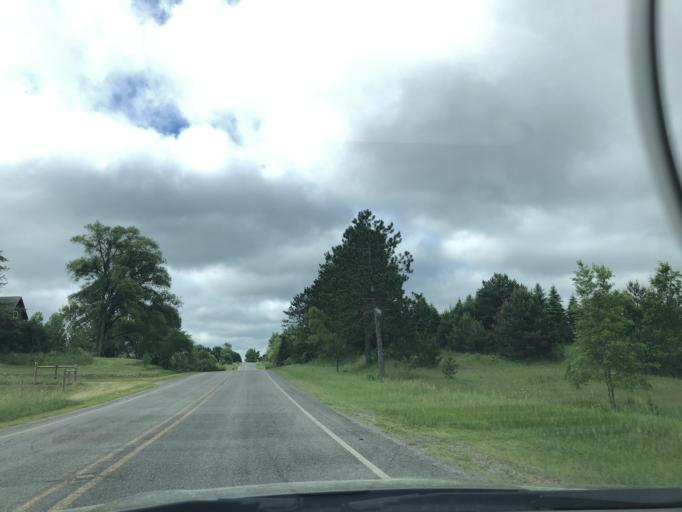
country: US
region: Michigan
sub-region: Missaukee County
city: Lake City
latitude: 44.4444
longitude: -85.2165
